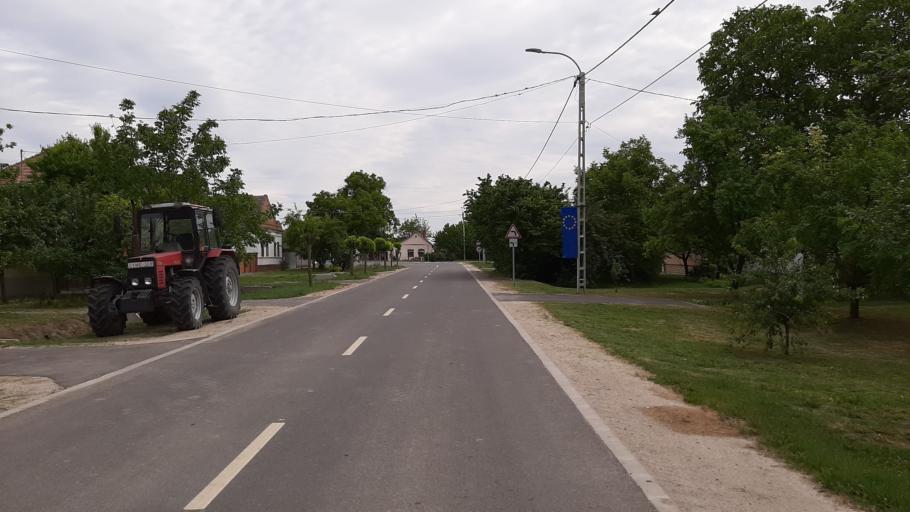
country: RO
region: Timis
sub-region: Comuna Beba Veche
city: Beba Veche
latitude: 46.1456
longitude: 20.2746
